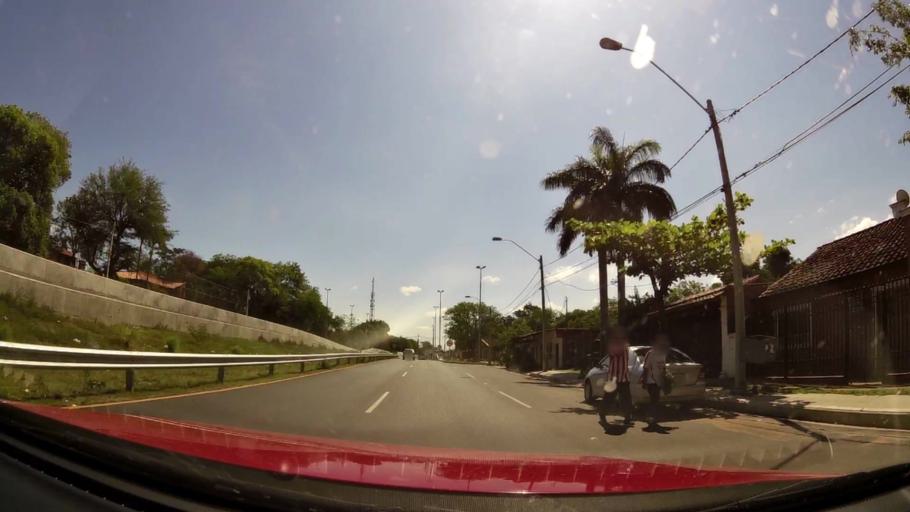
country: PY
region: Asuncion
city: Asuncion
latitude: -25.2564
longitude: -57.5637
